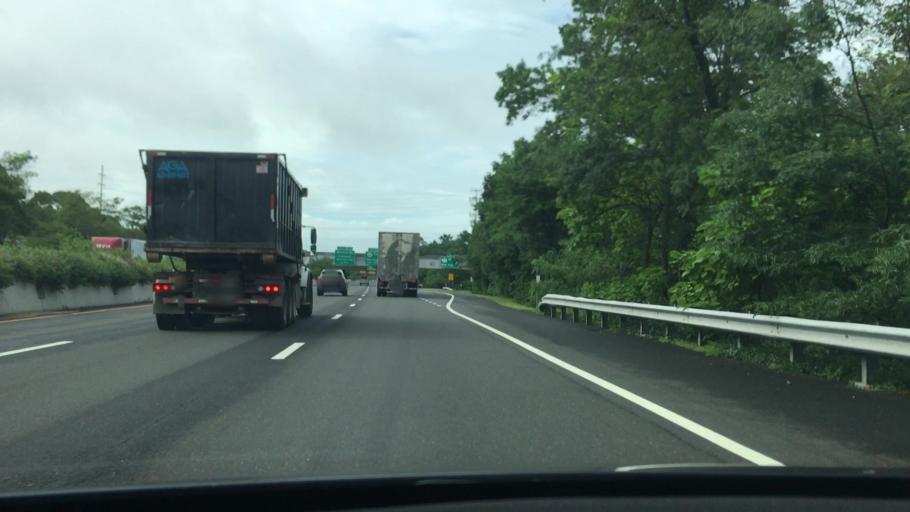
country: US
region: New York
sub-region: Nassau County
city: Seaford
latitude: 40.6769
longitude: -73.4945
